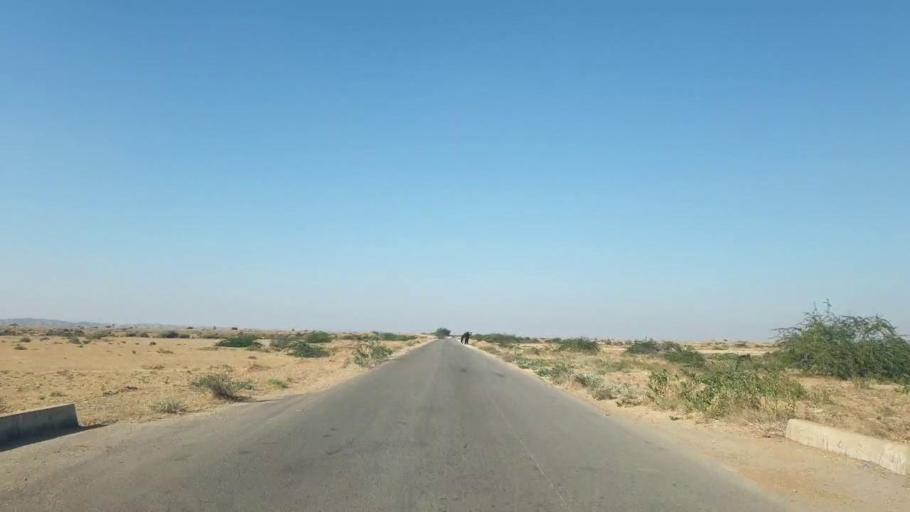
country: PK
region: Sindh
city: Malir Cantonment
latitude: 25.2532
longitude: 67.6029
